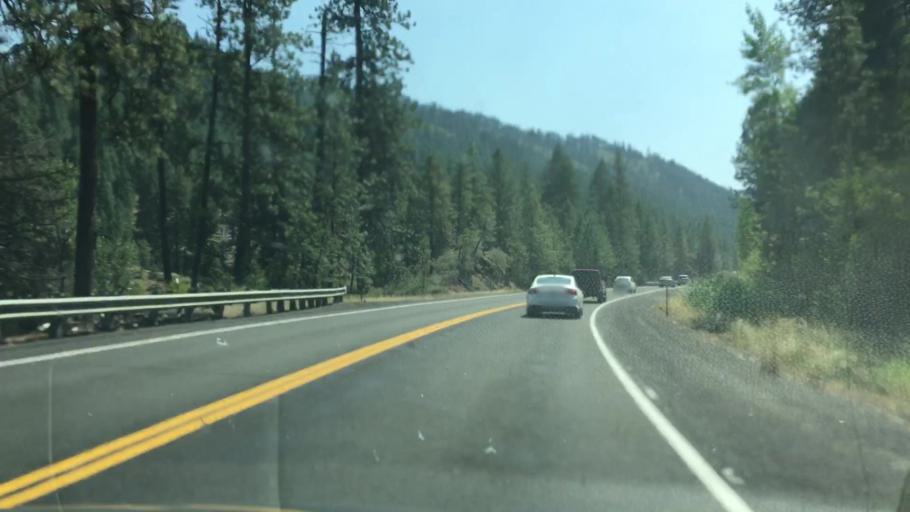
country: US
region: Idaho
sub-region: Valley County
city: McCall
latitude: 45.1851
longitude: -116.3021
